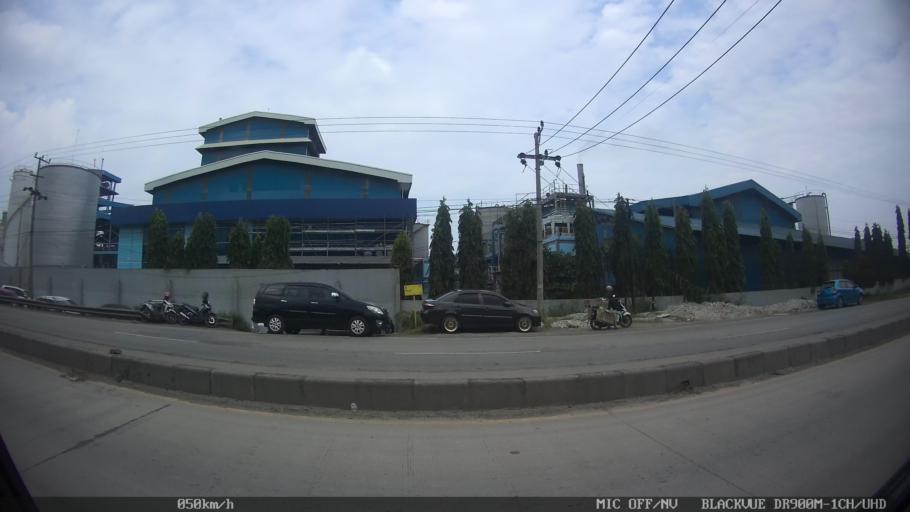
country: ID
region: Lampung
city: Panjang
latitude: -5.4570
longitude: 105.3160
